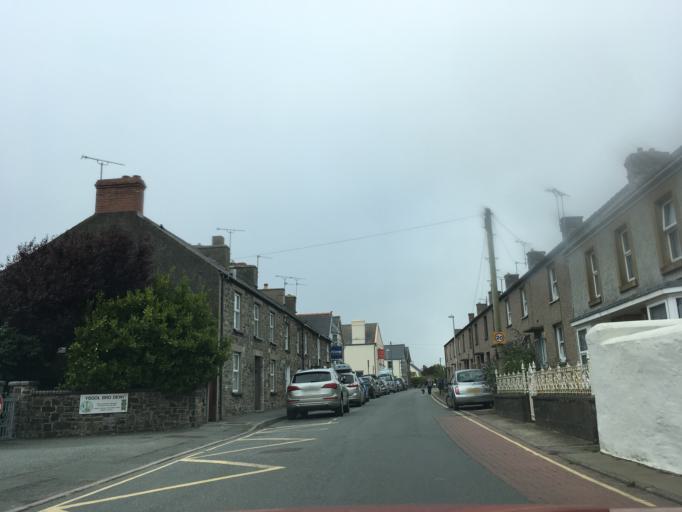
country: GB
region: Wales
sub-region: Pembrokeshire
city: Saint David's
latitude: 51.8830
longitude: -5.2645
